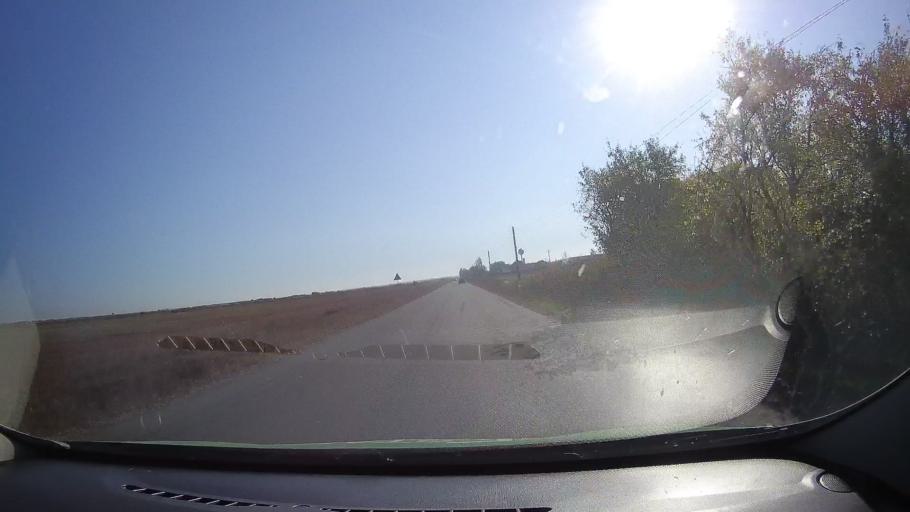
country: RO
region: Satu Mare
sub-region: Comuna Santau
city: Santau
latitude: 47.5085
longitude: 22.5216
